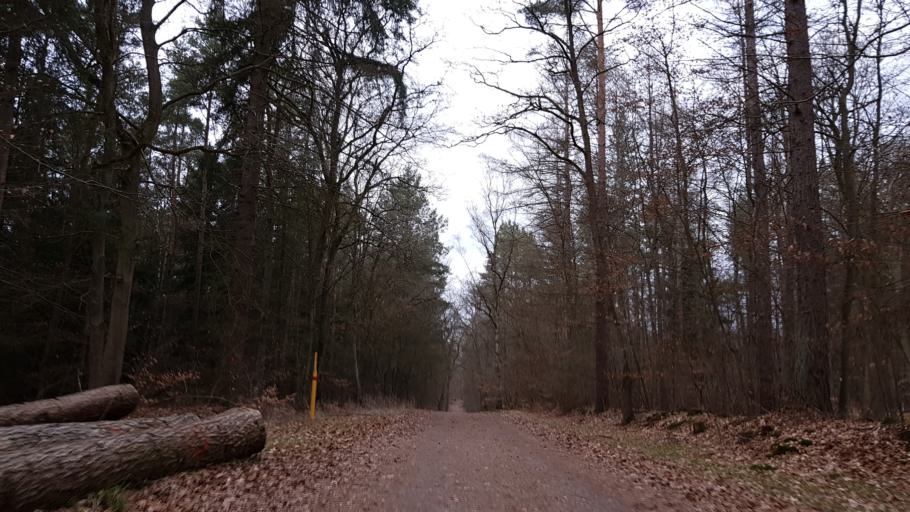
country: DE
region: Lower Saxony
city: Deutsch Evern
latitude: 53.2173
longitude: 10.4247
